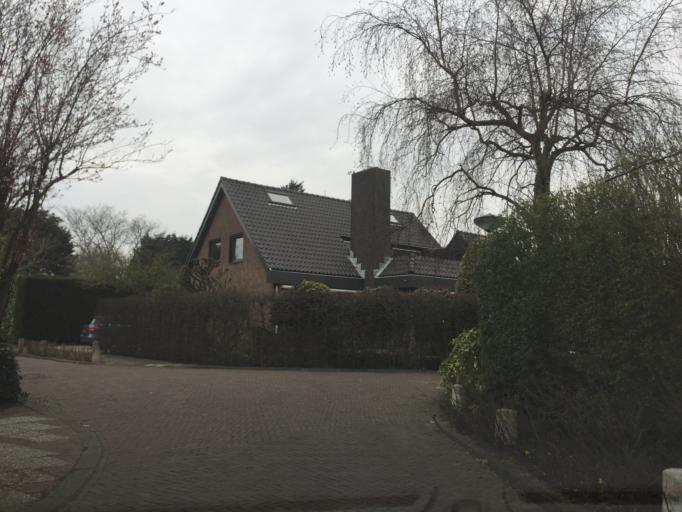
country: NL
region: South Holland
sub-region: Gemeente Leiderdorp
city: Leiderdorp
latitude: 52.1732
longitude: 4.5155
